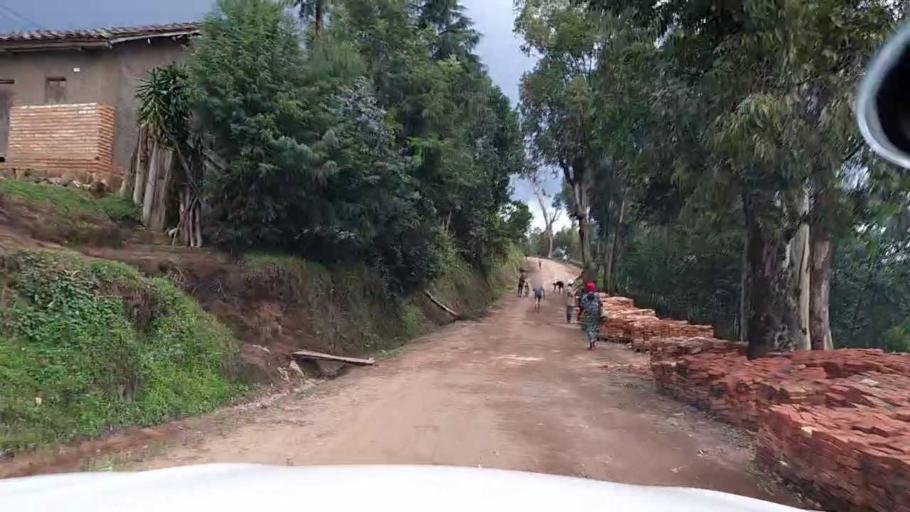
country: BI
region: Kayanza
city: Kayanza
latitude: -2.7912
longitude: 29.5210
